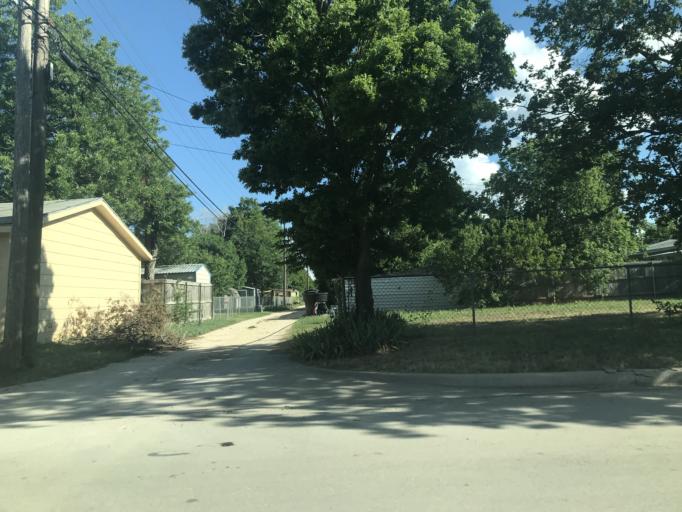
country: US
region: Texas
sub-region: Taylor County
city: Abilene
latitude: 32.4360
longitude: -99.7850
